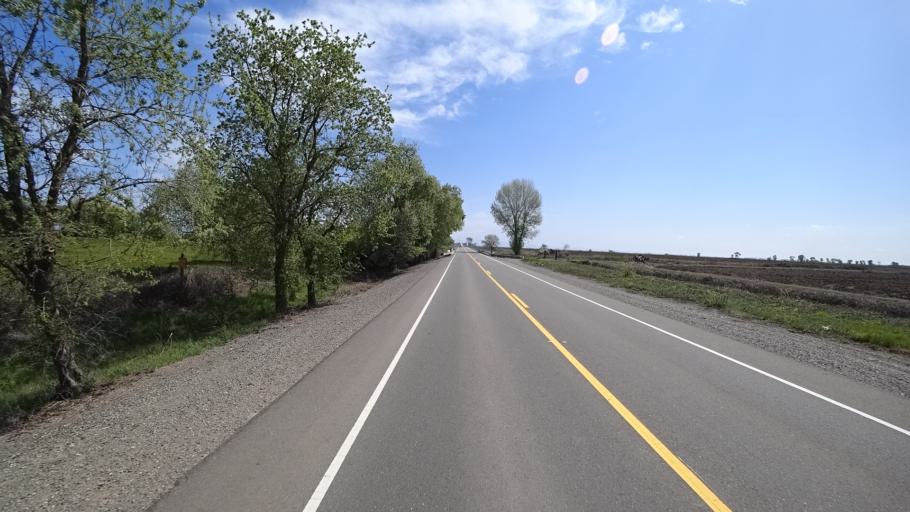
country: US
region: California
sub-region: Butte County
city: Biggs
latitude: 39.4641
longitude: -121.8669
